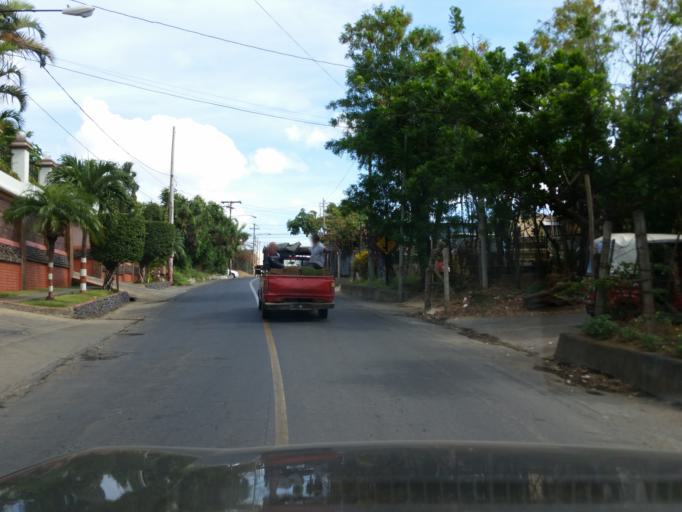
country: NI
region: Managua
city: Managua
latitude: 12.0897
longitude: -86.2447
